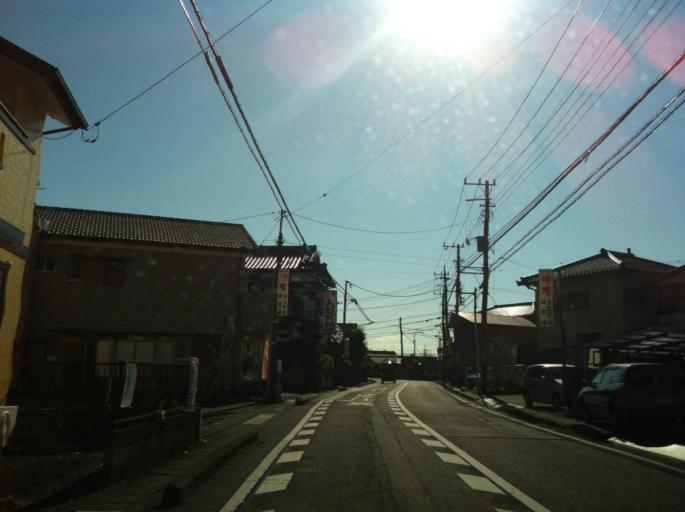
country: JP
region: Shizuoka
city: Fuji
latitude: 35.1646
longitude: 138.7319
